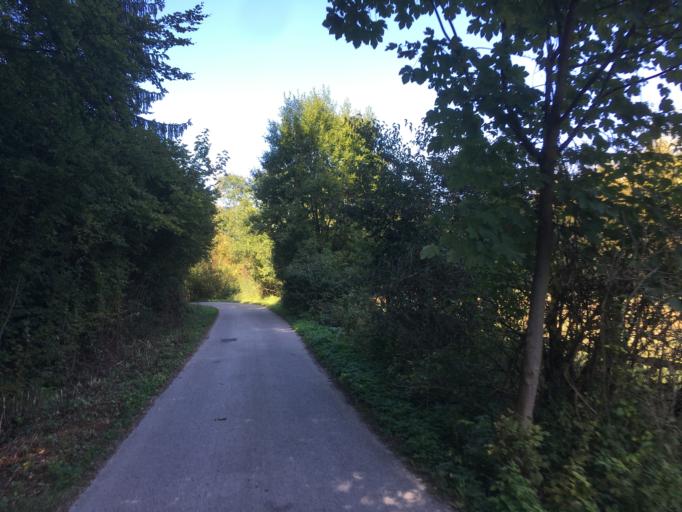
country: SK
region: Trenciansky
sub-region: Okres Povazska Bystrica
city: Povazska Bystrica
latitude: 49.0283
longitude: 18.4354
